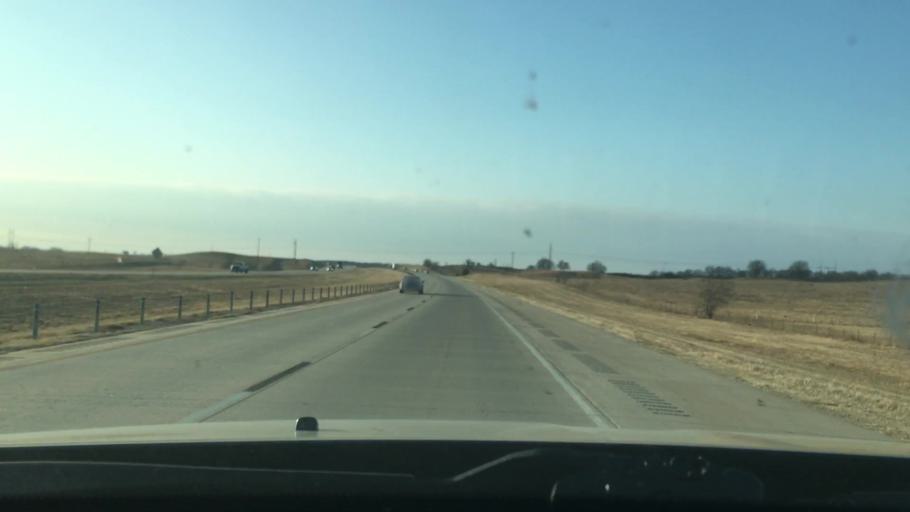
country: US
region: Oklahoma
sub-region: Carter County
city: Ardmore
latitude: 34.2603
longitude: -97.1651
